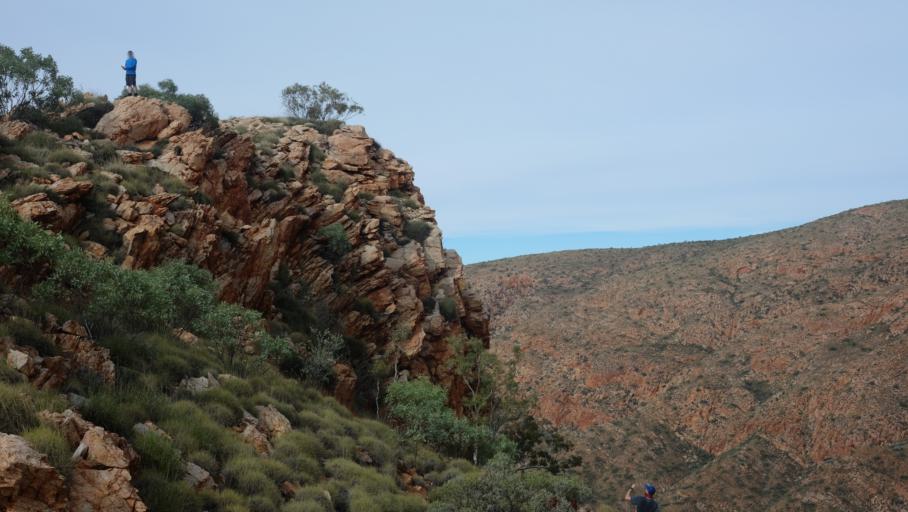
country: AU
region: Northern Territory
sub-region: Alice Springs
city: Alice Springs
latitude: -23.7120
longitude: 133.4288
